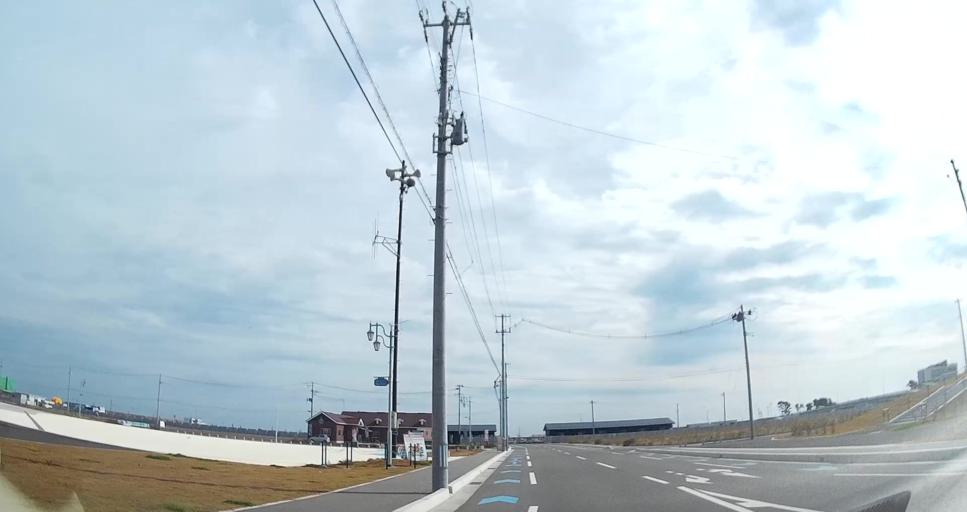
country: JP
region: Miyagi
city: Iwanuma
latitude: 38.1719
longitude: 140.9545
